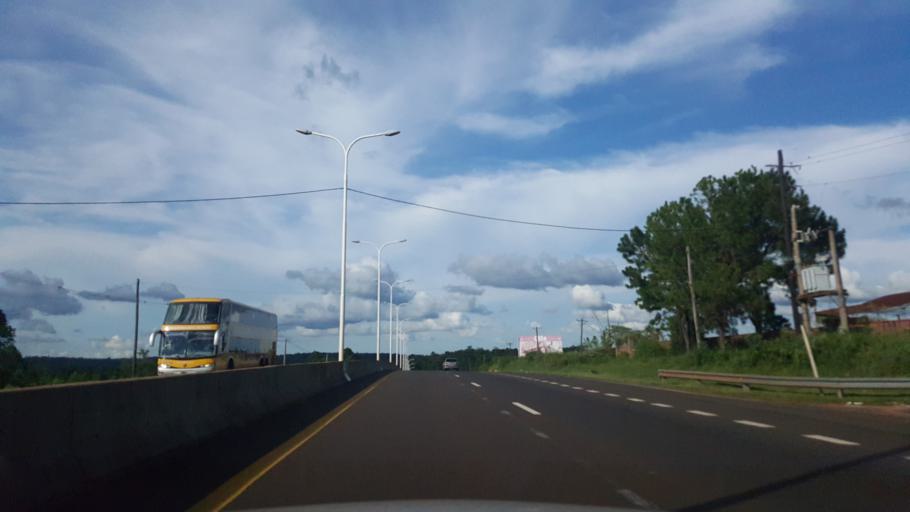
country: AR
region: Misiones
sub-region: Departamento de Candelaria
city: Loreto
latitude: -27.3003
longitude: -55.5371
